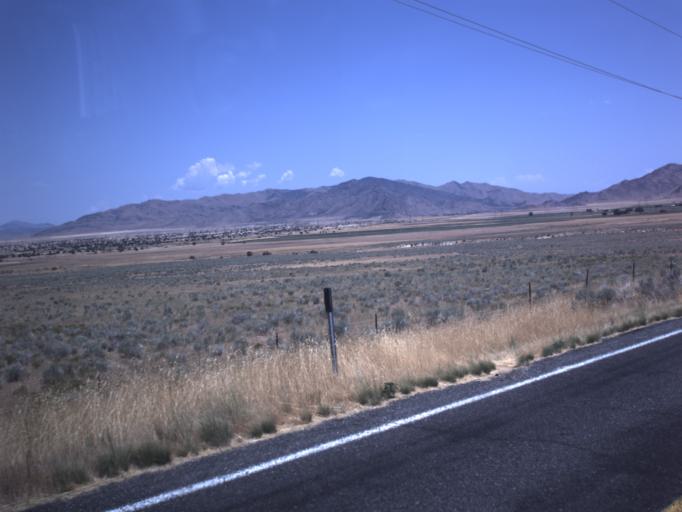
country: US
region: Utah
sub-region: Millard County
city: Delta
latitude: 39.4542
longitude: -112.3027
